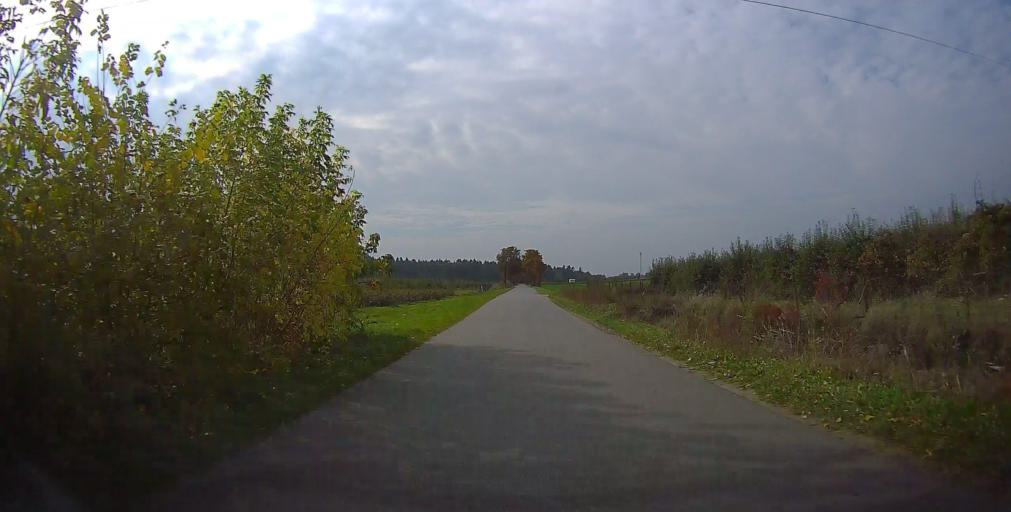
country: PL
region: Masovian Voivodeship
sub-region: Powiat bialobrzeski
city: Wysmierzyce
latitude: 51.6494
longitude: 20.7642
